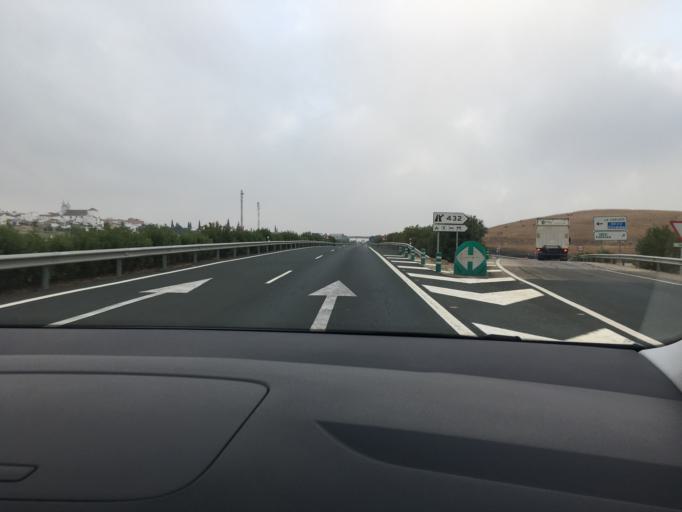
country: ES
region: Andalusia
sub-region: Province of Cordoba
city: La Carlota
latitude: 37.6803
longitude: -4.9294
